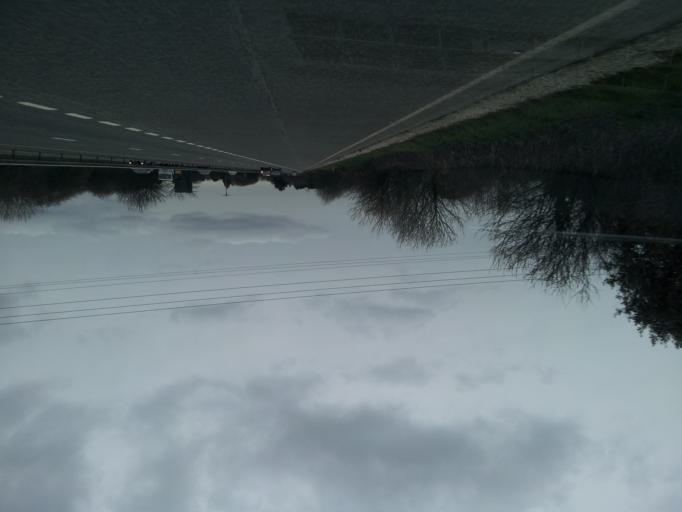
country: GB
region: England
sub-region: Cornwall
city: Redruth
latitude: 50.2458
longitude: -5.2306
